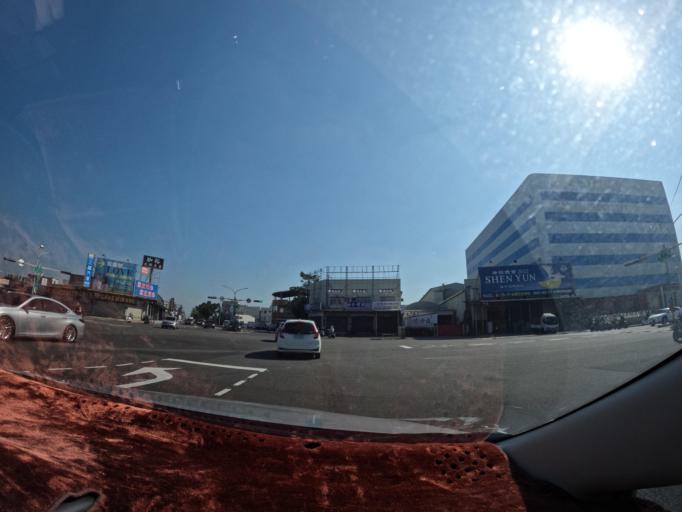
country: TW
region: Taiwan
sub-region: Tainan
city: Tainan
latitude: 22.9973
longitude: 120.2578
